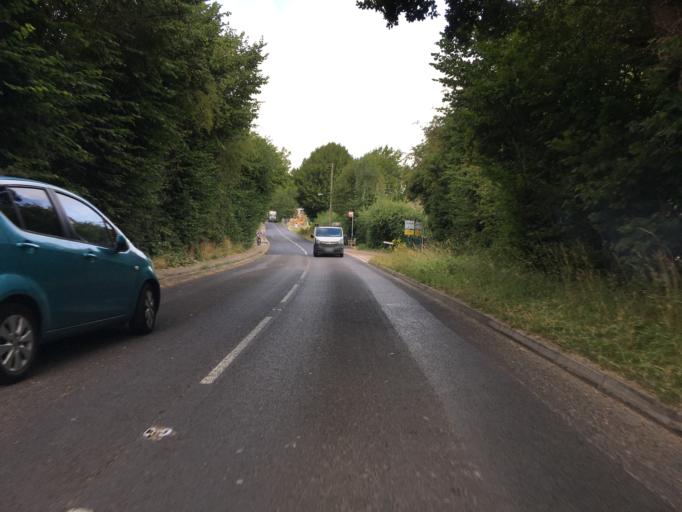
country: GB
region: England
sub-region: Kent
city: Cranbrook
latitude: 51.1106
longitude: 0.5590
